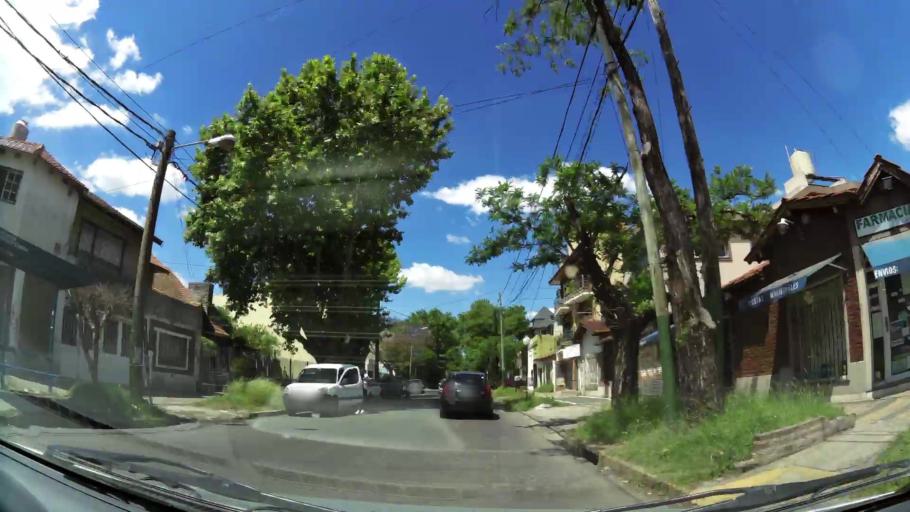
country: AR
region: Buenos Aires
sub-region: Partido de Lomas de Zamora
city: Lomas de Zamora
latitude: -34.7386
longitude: -58.4082
